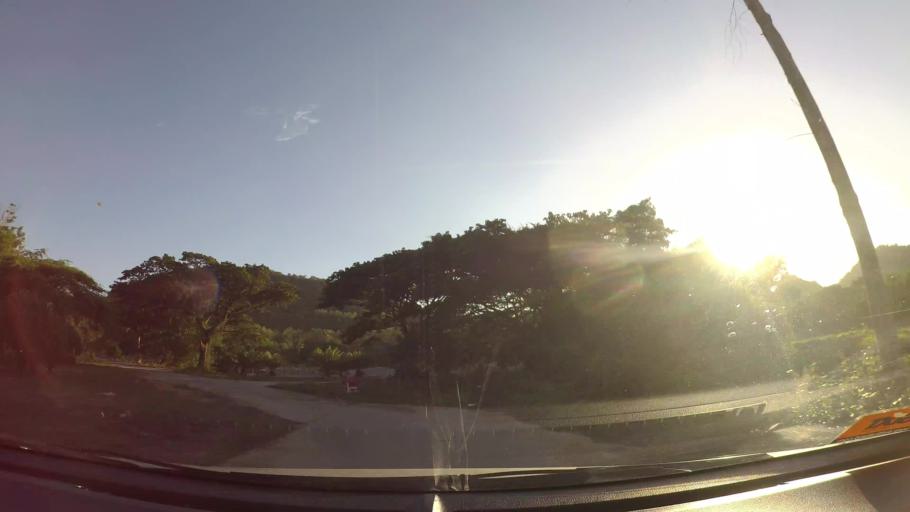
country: TH
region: Chon Buri
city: Si Racha
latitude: 13.1376
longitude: 100.9292
